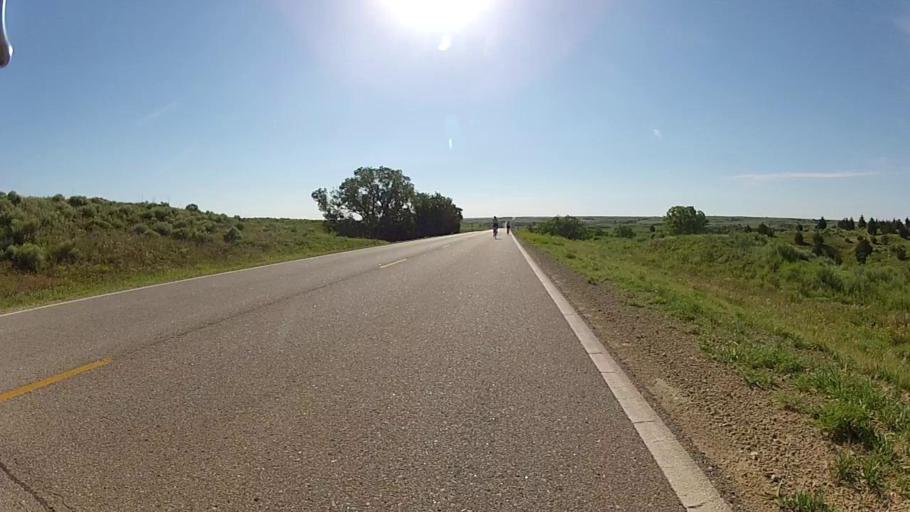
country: US
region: Kansas
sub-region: Barber County
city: Medicine Lodge
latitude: 37.2817
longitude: -98.8869
